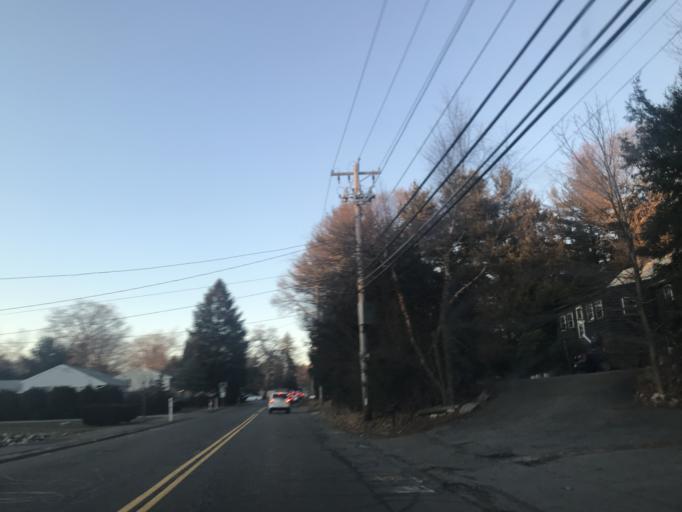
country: US
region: Massachusetts
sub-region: Essex County
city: Saugus
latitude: 42.4789
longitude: -71.0098
